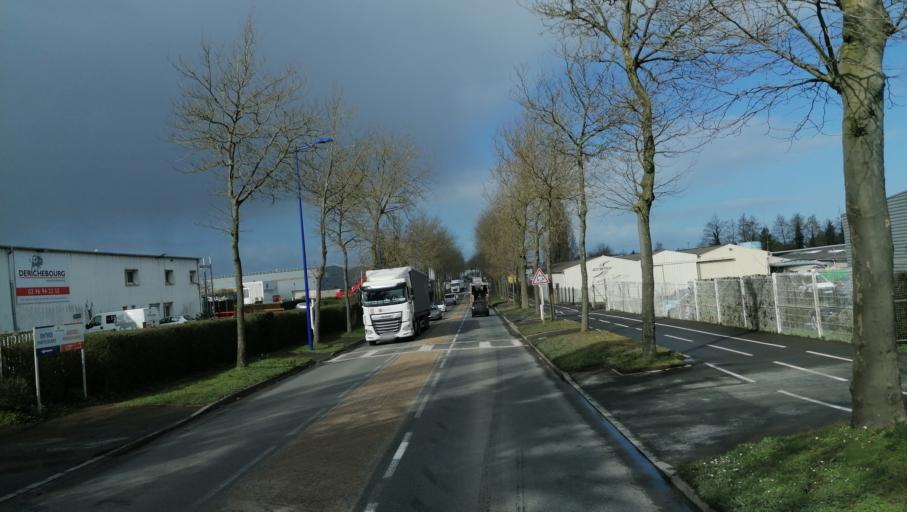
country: FR
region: Brittany
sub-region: Departement des Cotes-d'Armor
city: Ploufragan
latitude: 48.4658
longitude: -2.7887
